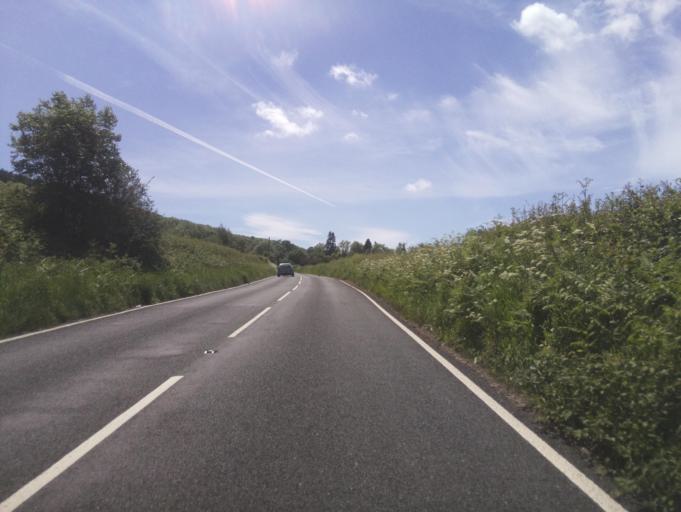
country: GB
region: Wales
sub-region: Monmouthshire
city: Mitchel Troy
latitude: 51.7854
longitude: -2.7183
